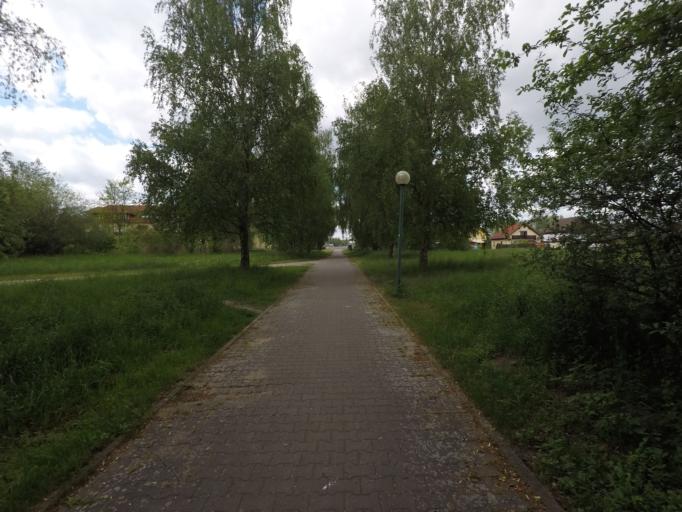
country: DE
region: Brandenburg
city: Melchow
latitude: 52.8460
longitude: 13.6959
